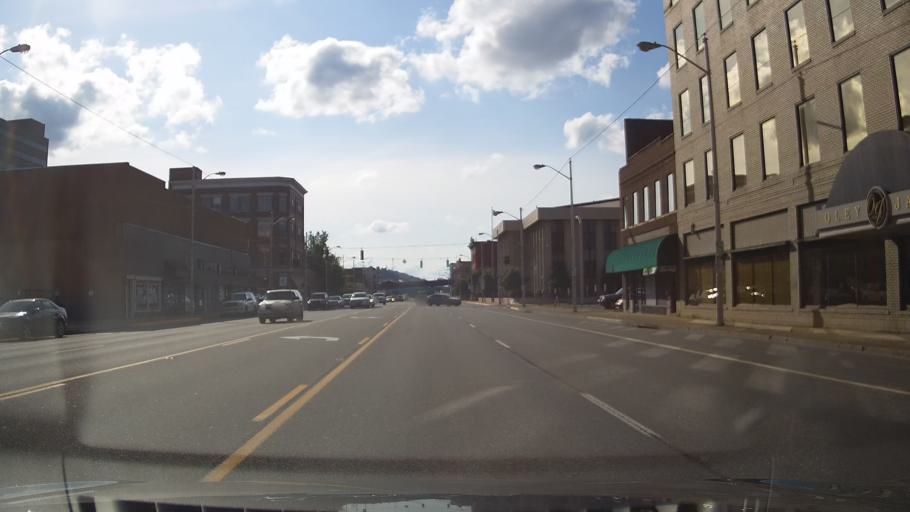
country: US
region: Kentucky
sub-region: Boyd County
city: Ashland
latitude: 38.4797
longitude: -82.6390
